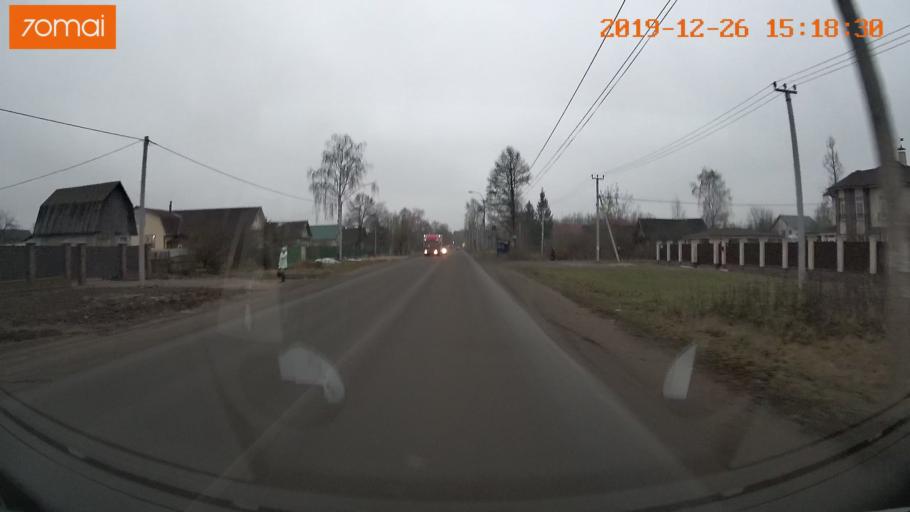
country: RU
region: Jaroslavl
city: Rybinsk
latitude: 58.0694
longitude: 38.8444
